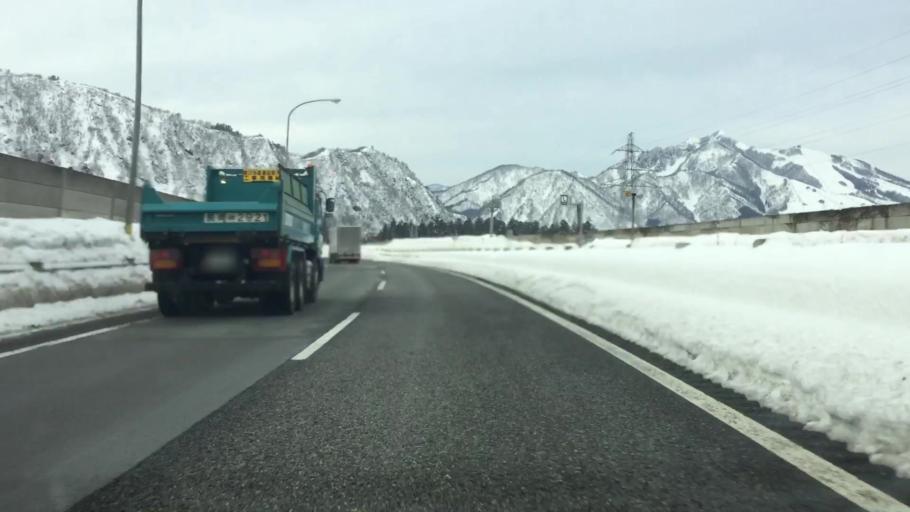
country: JP
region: Niigata
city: Shiozawa
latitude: 36.9049
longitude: 138.8468
